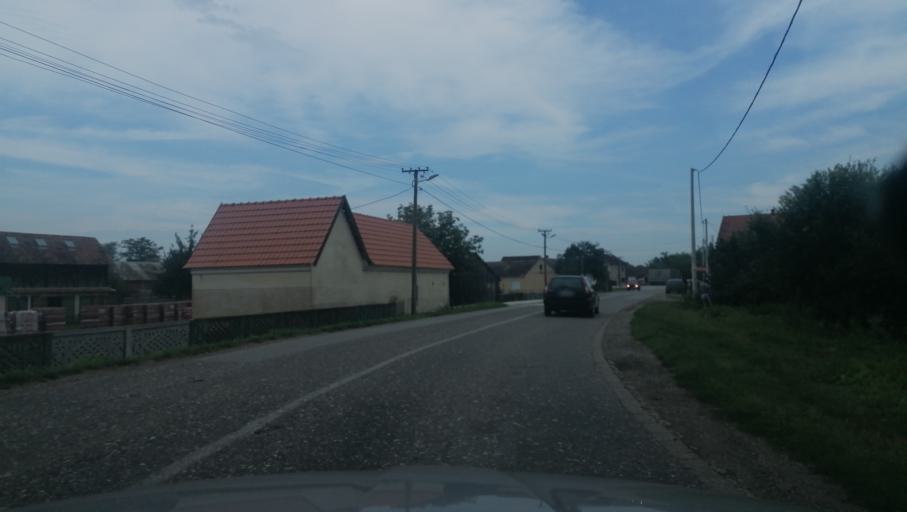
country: RS
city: Klenje
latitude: 44.8082
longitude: 19.4344
